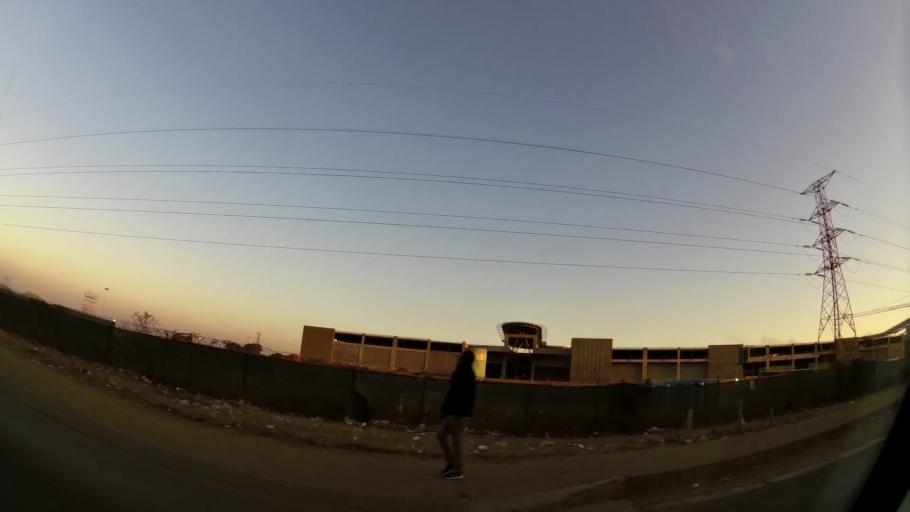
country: ZA
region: Gauteng
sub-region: City of Tshwane Metropolitan Municipality
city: Pretoria
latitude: -25.7185
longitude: 28.3418
